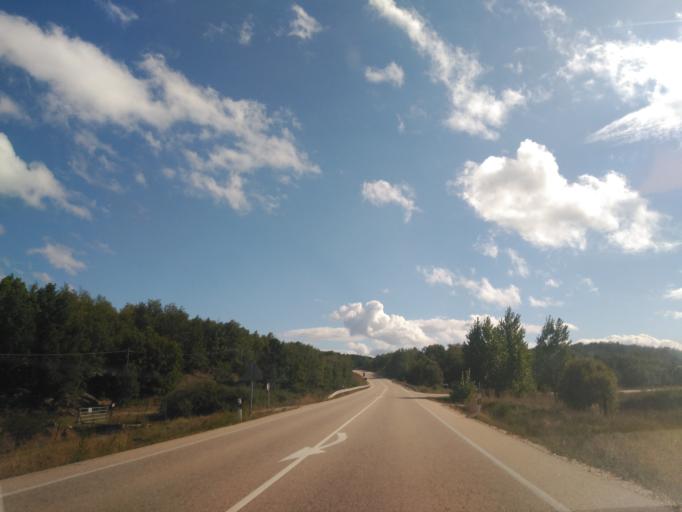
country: ES
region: Castille and Leon
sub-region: Provincia de Burgos
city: Pinilla de los Barruecos
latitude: 41.9209
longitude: -3.2793
